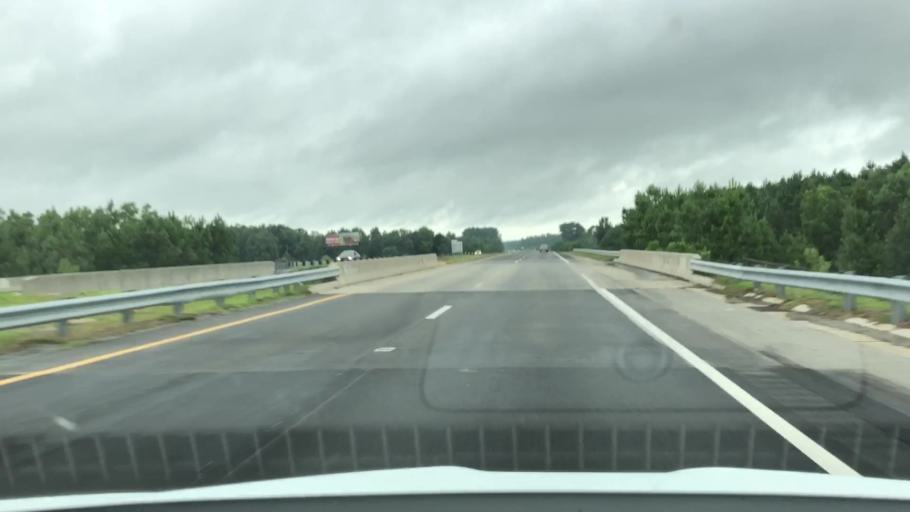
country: US
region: North Carolina
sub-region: Wayne County
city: Goldsboro
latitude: 35.4420
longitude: -77.9843
